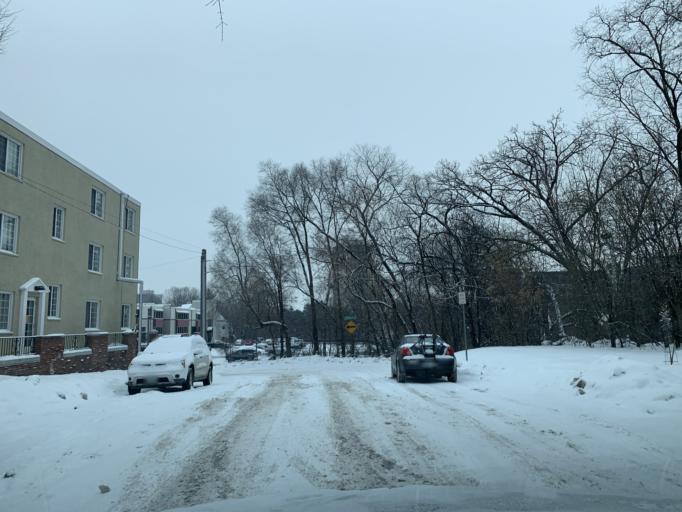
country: US
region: Minnesota
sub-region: Hennepin County
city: Saint Louis Park
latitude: 44.9466
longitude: -93.3282
